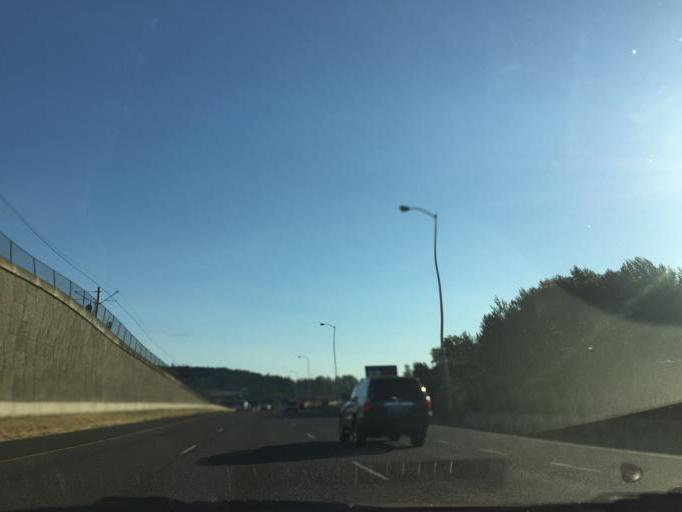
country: US
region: Oregon
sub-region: Multnomah County
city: Lents
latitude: 45.5654
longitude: -122.5574
